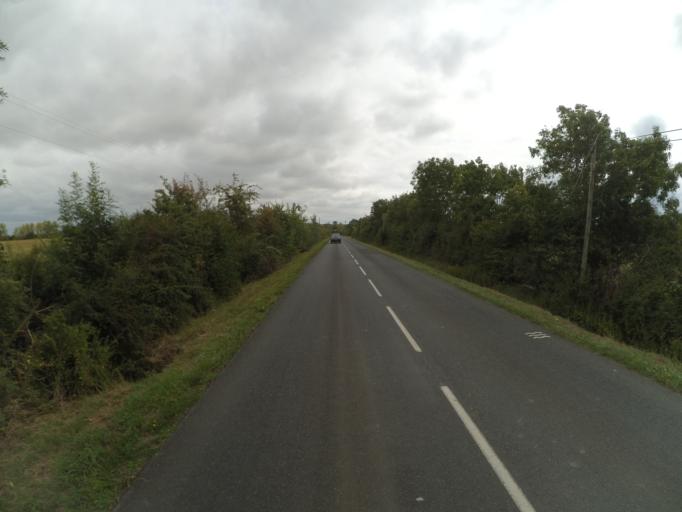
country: FR
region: Pays de la Loire
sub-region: Departement de la Vendee
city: Les Magnils-Reigniers
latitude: 46.4340
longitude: -1.2722
